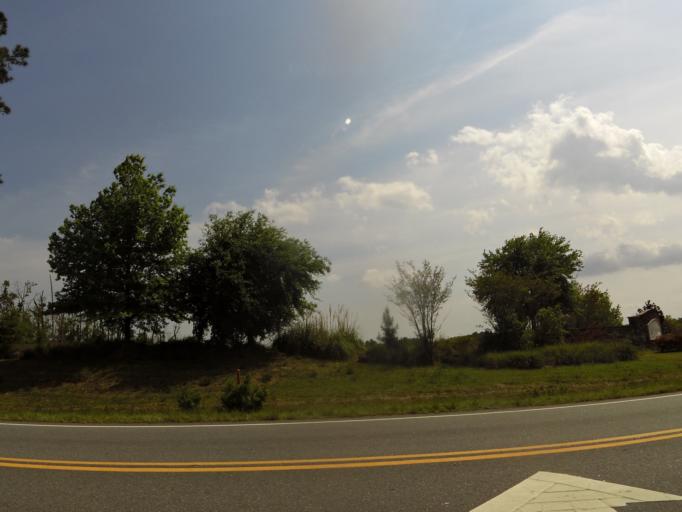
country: US
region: Georgia
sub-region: Camden County
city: Kingsland
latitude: 30.8101
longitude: -81.7816
